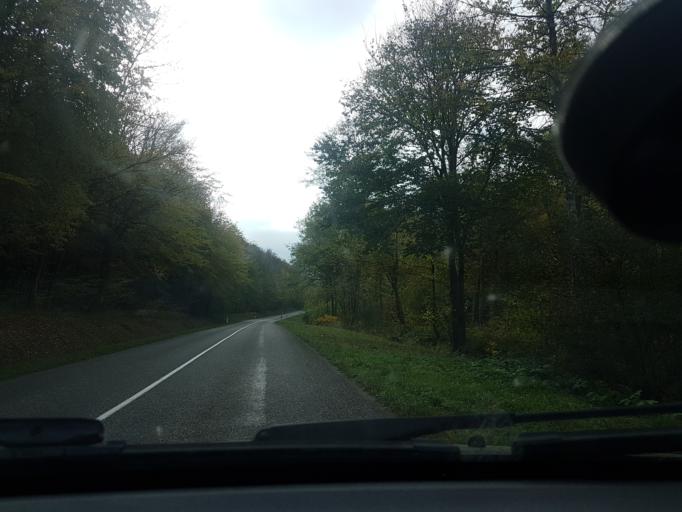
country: FR
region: Franche-Comte
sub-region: Territoire de Belfort
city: Essert
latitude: 47.6470
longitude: 6.8115
